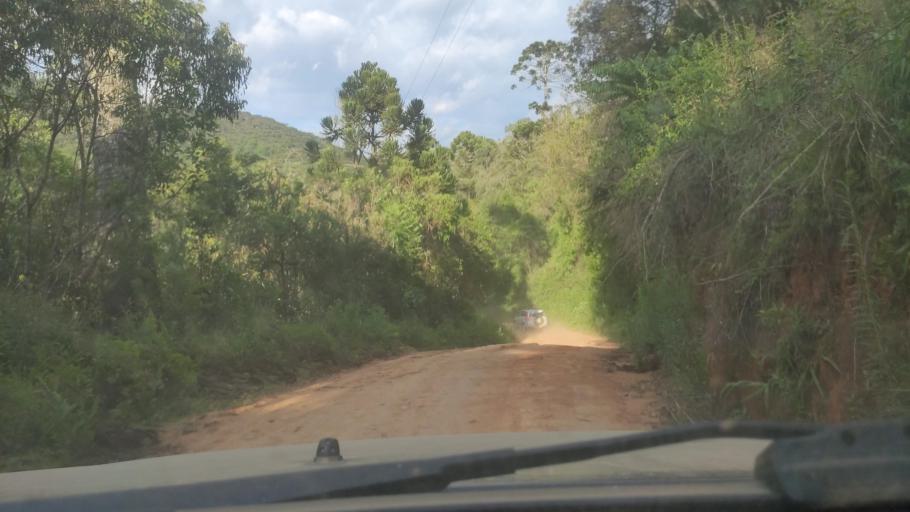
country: BR
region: Minas Gerais
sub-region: Cambui
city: Cambui
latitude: -22.7569
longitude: -45.9495
